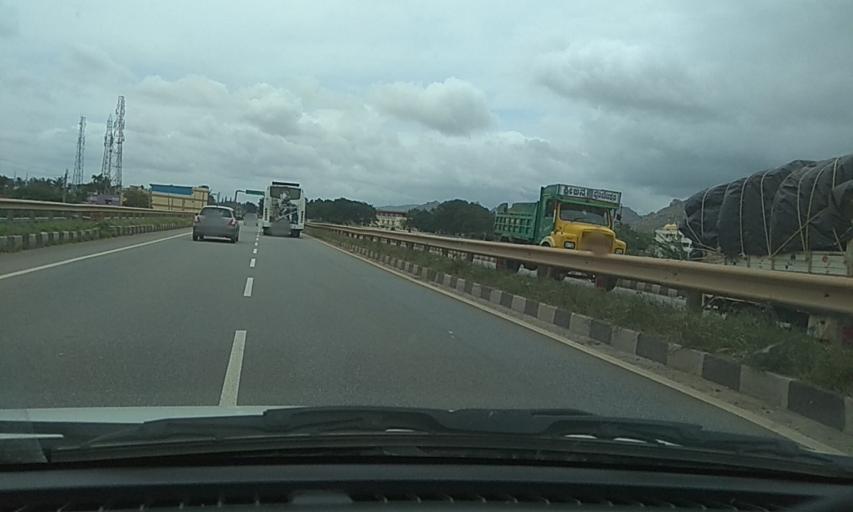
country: IN
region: Karnataka
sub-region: Chitradurga
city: Chitradurga
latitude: 14.2403
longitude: 76.3745
